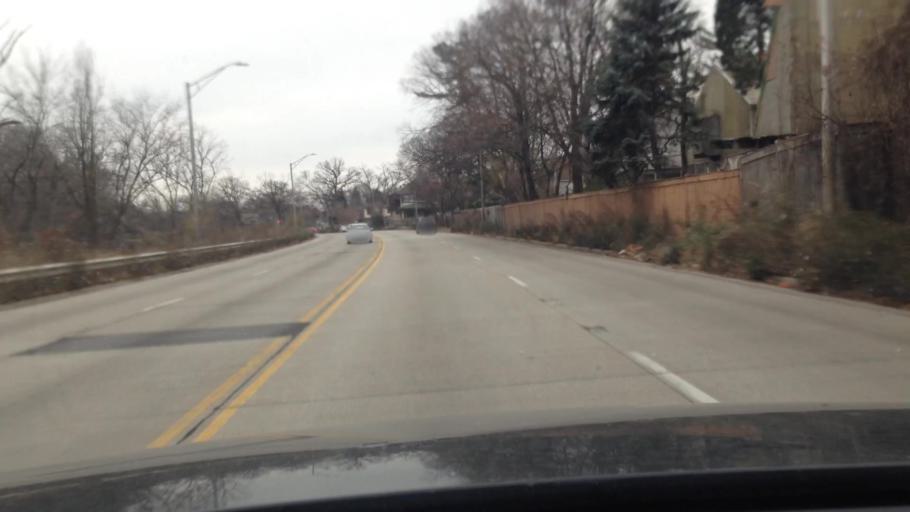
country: US
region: Illinois
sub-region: Cook County
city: Maywood
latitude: 41.8970
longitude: -87.8353
